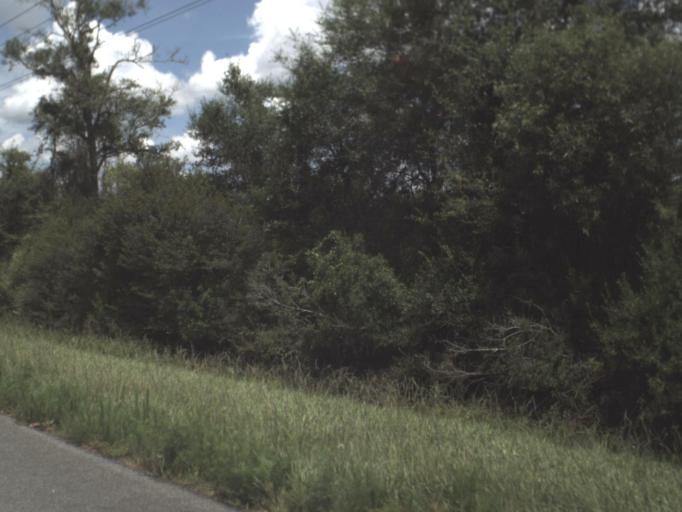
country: US
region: Florida
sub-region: Taylor County
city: Perry
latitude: 30.0947
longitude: -83.6856
